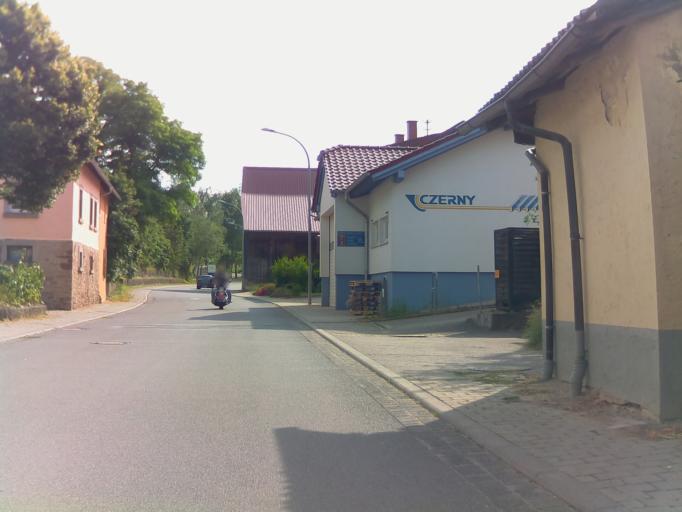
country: DE
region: Baden-Wuerttemberg
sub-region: Regierungsbezirk Stuttgart
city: Buch am Ahorn
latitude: 49.5342
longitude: 9.5042
